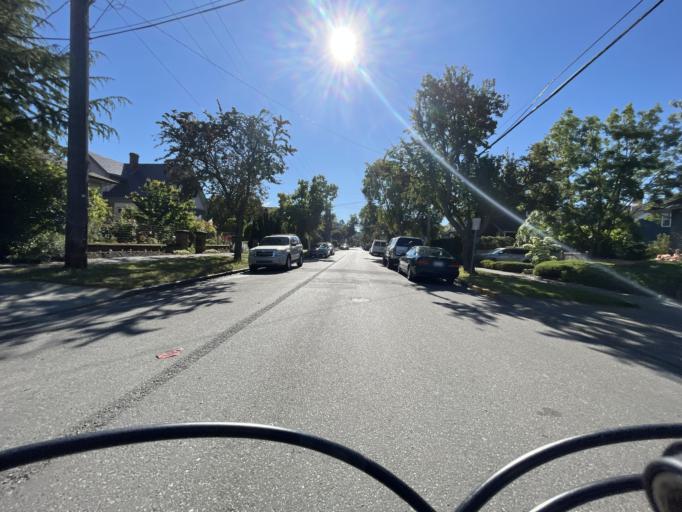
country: CA
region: British Columbia
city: Victoria
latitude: 48.4195
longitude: -123.3539
